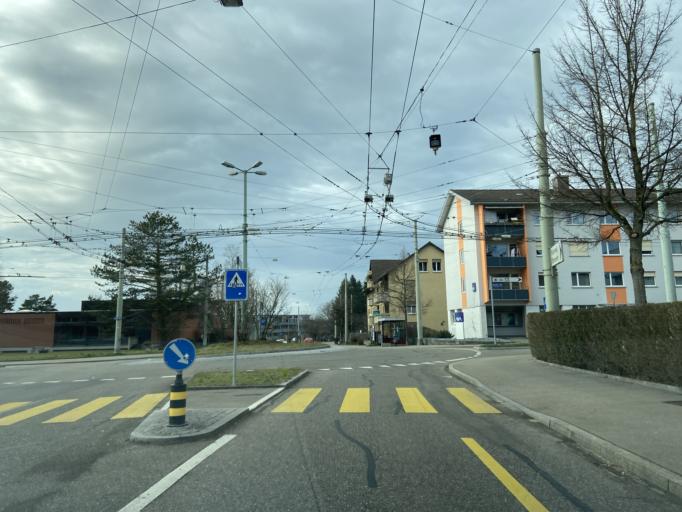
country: CH
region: Zurich
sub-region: Bezirk Winterthur
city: Seen (Kreis 3) / Bueelwiesen
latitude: 47.4859
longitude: 8.7655
